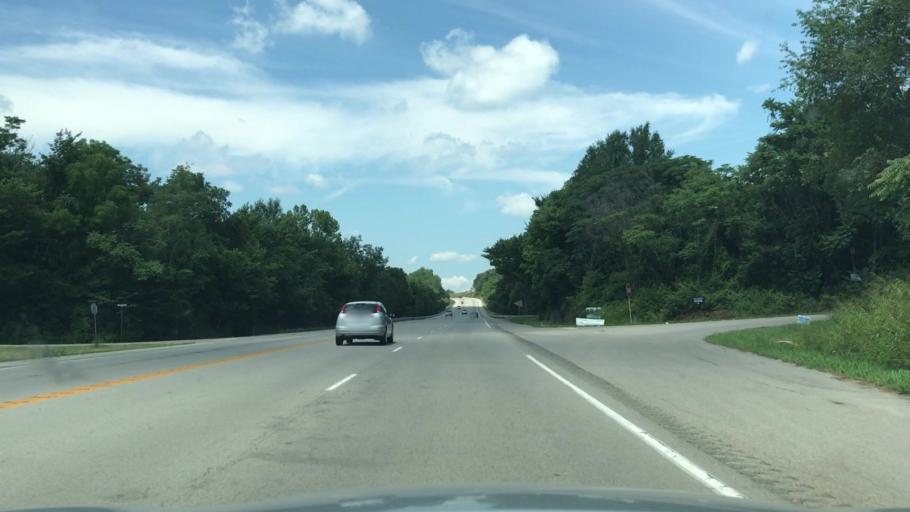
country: US
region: Kentucky
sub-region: Wayne County
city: Monticello
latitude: 36.7643
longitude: -84.9870
